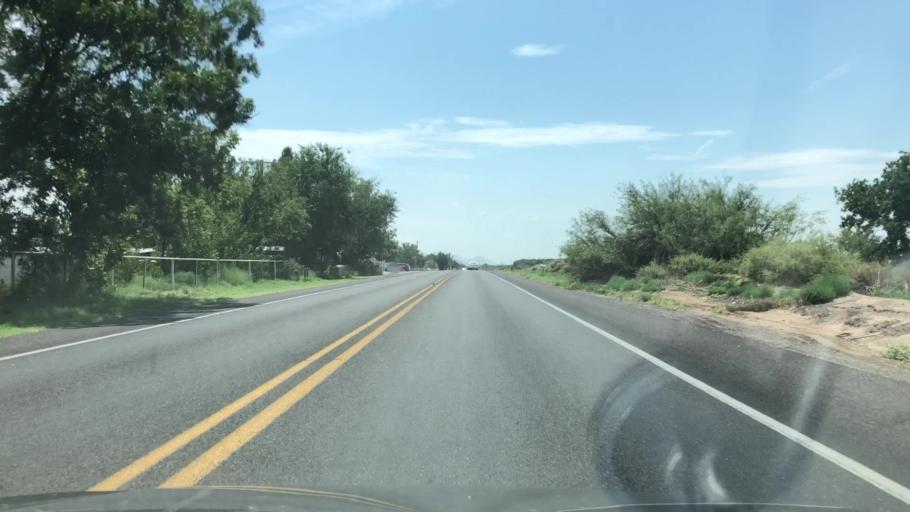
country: US
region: New Mexico
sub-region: Dona Ana County
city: Mesquite
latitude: 32.2010
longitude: -106.7197
